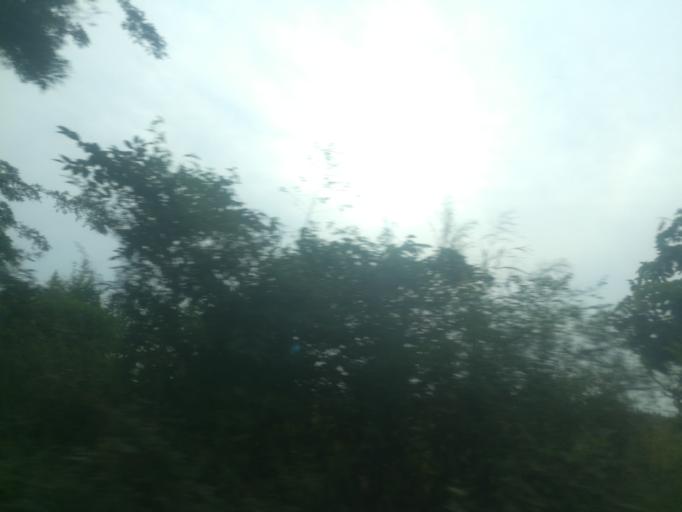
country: NG
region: Ogun
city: Ayetoro
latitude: 7.2605
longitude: 3.1114
